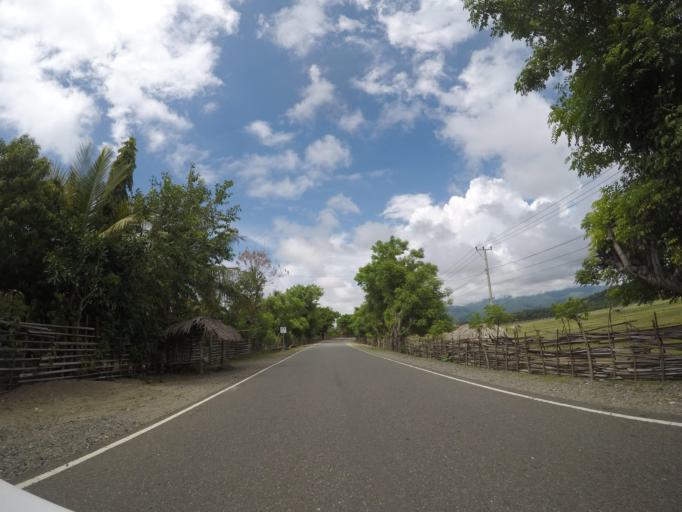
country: TL
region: Liquica
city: Maubara
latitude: -8.7594
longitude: 125.1004
